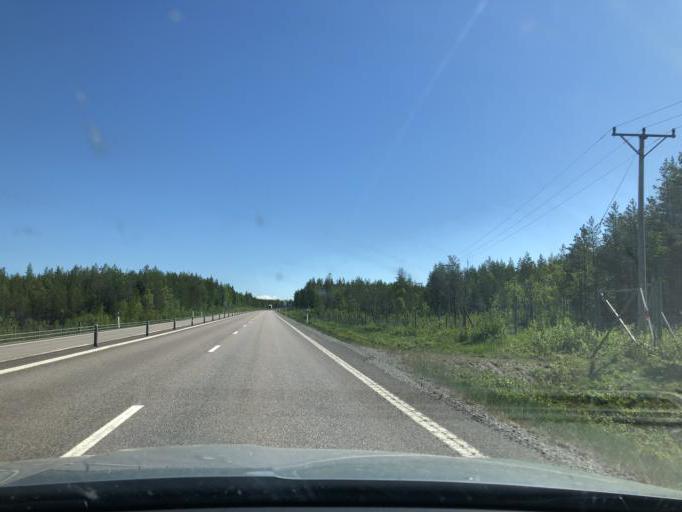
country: SE
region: Norrbotten
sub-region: Kalix Kommun
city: Toere
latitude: 65.9167
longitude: 22.7400
